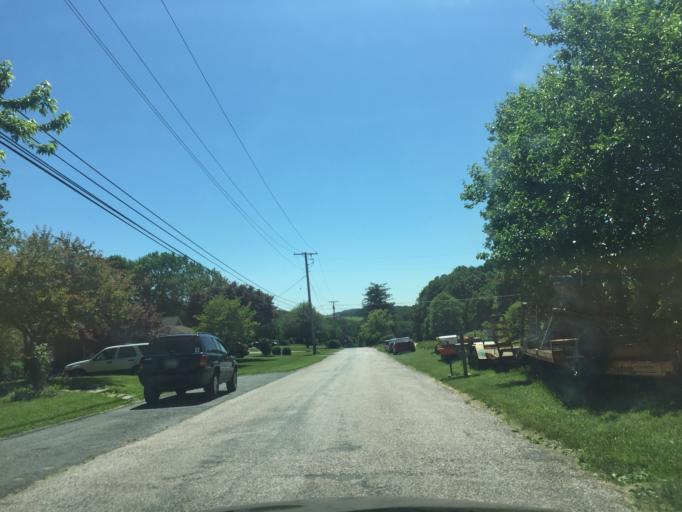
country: US
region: Maryland
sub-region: Carroll County
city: Manchester
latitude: 39.6572
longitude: -76.8972
